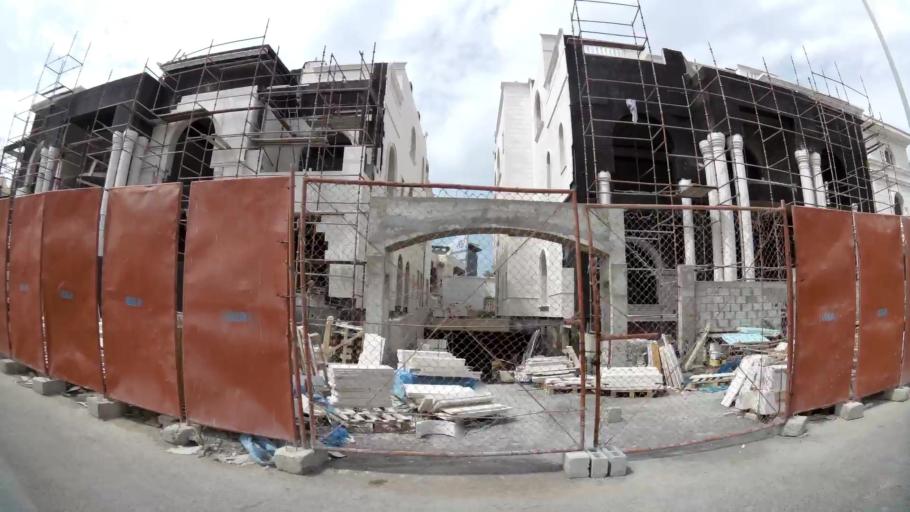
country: AE
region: Abu Dhabi
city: Abu Dhabi
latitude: 24.4632
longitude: 54.3375
